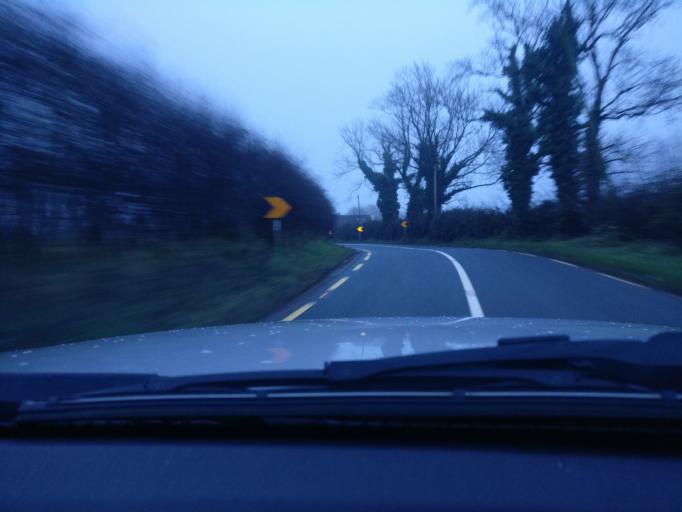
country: IE
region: Leinster
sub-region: An Mhi
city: Athboy
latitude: 53.6072
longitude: -6.9721
